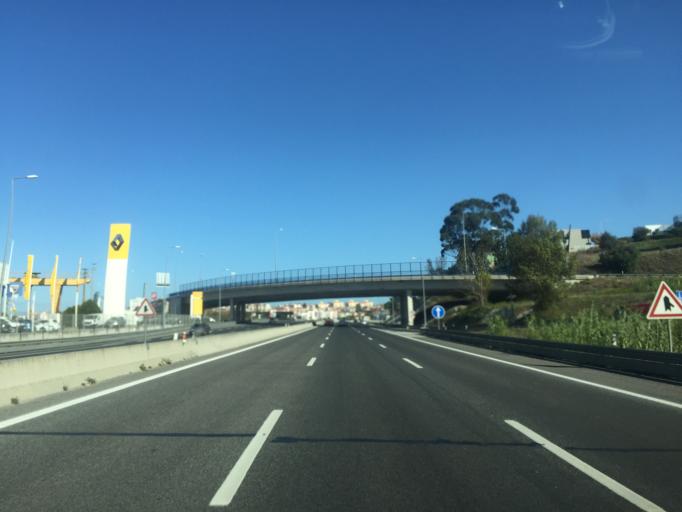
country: PT
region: Leiria
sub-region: Leiria
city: Leiria
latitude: 39.7447
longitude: -8.8191
